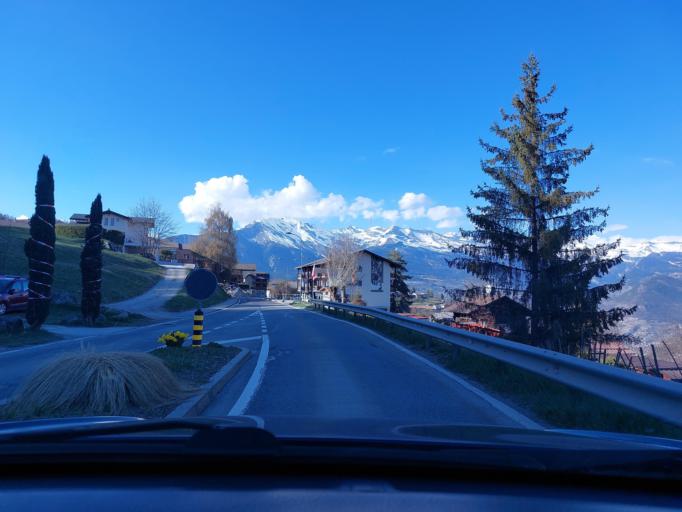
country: CH
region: Valais
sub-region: Herens District
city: Vex
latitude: 46.2063
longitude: 7.4017
